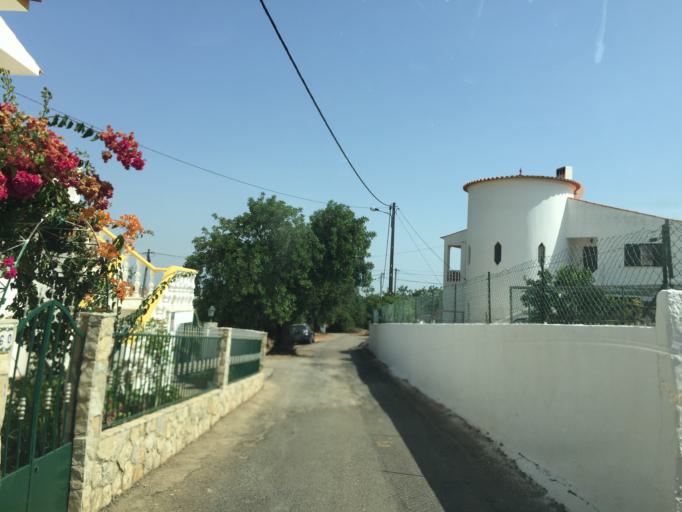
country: PT
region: Faro
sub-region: Loule
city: Boliqueime
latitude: 37.1203
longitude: -8.1957
